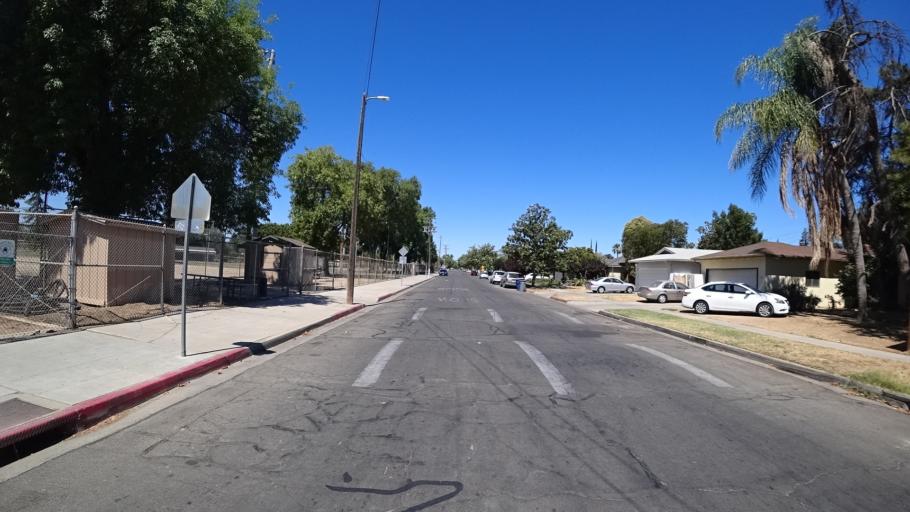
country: US
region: California
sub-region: Fresno County
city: Fresno
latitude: 36.7884
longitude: -119.8198
